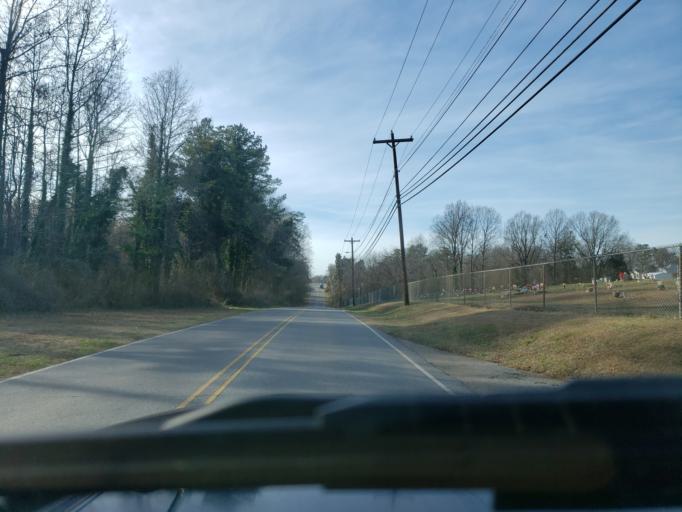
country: US
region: North Carolina
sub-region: Cleveland County
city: Kings Mountain
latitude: 35.2376
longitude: -81.3367
